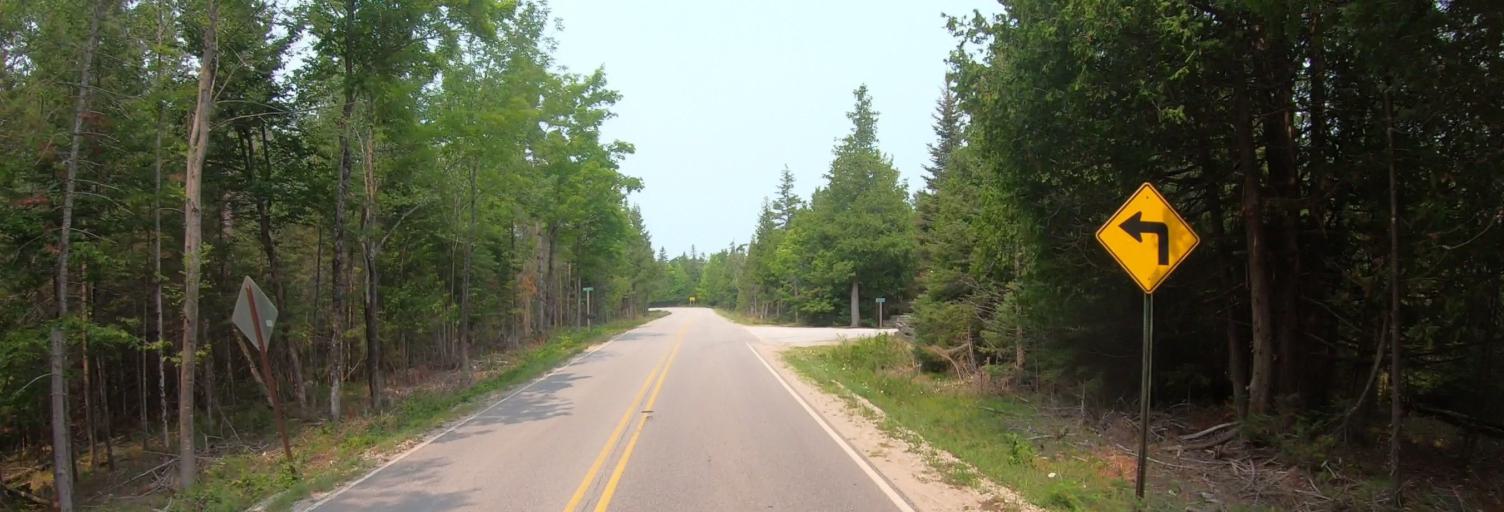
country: CA
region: Ontario
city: Thessalon
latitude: 46.0146
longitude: -83.7075
